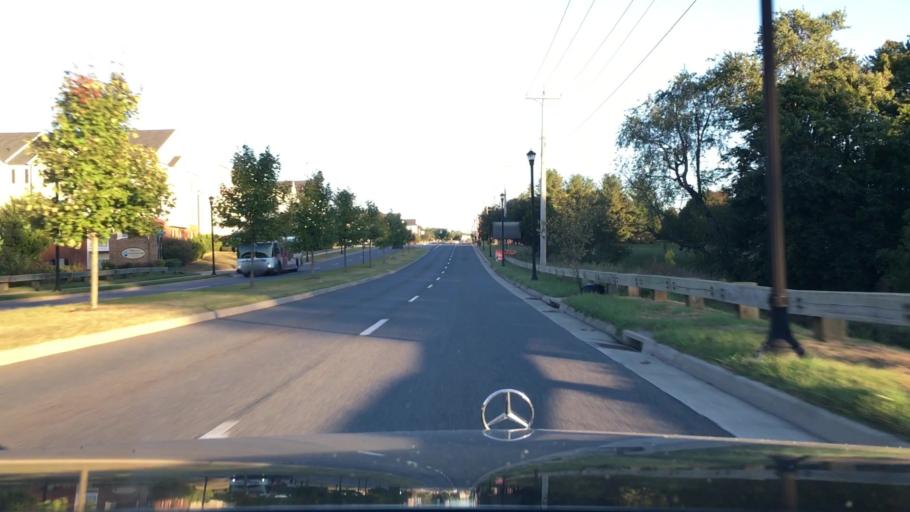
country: US
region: Virginia
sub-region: Campbell County
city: Timberlake
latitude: 37.3412
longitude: -79.2297
